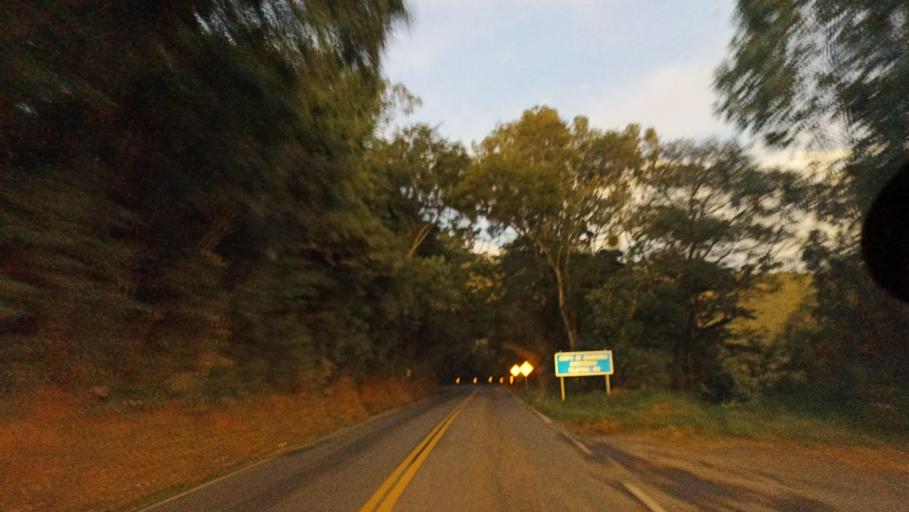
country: BR
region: Minas Gerais
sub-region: Sao Lourenco
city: Sao Lourenco
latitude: -22.1643
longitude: -44.9650
